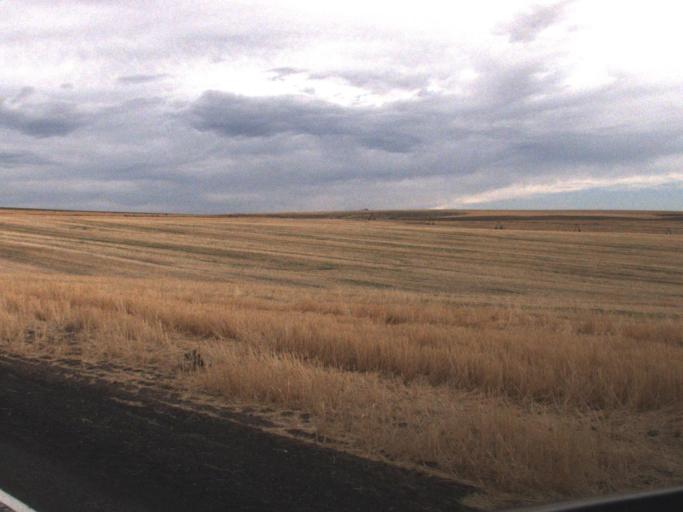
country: US
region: Washington
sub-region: Okanogan County
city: Coulee Dam
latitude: 47.6151
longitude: -118.7205
